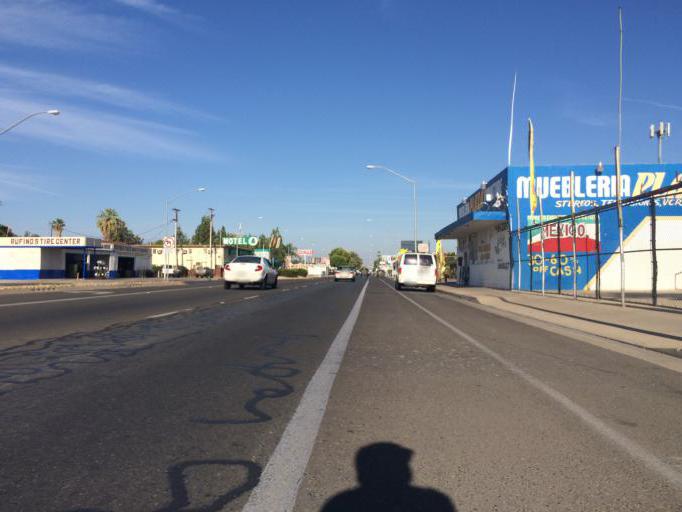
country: US
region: California
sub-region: Fresno County
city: Fresno
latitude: 36.7358
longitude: -119.7421
